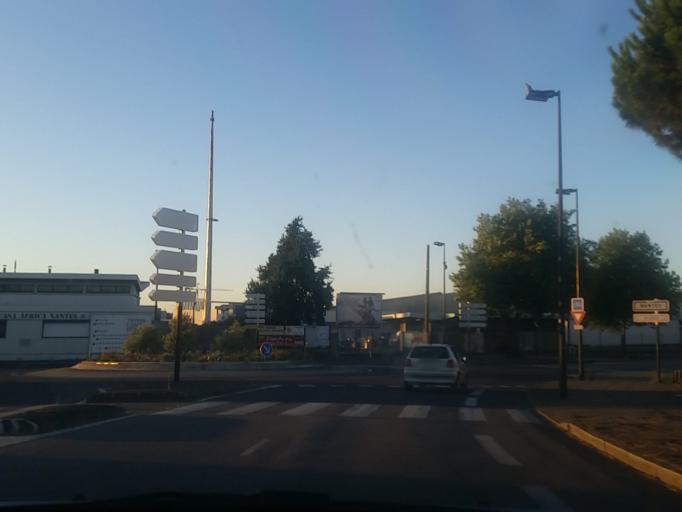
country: FR
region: Pays de la Loire
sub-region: Departement de la Loire-Atlantique
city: Nantes
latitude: 47.1996
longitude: -1.5615
